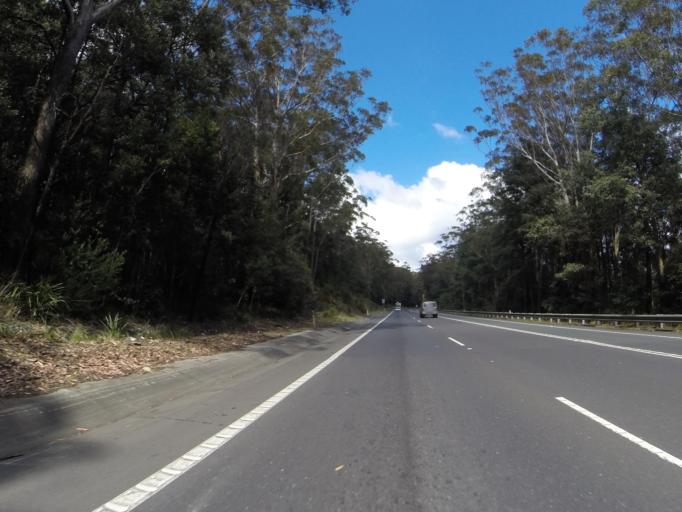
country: AU
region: New South Wales
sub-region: Wollongong
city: Mount Ousley
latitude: -34.3666
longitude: 150.8502
